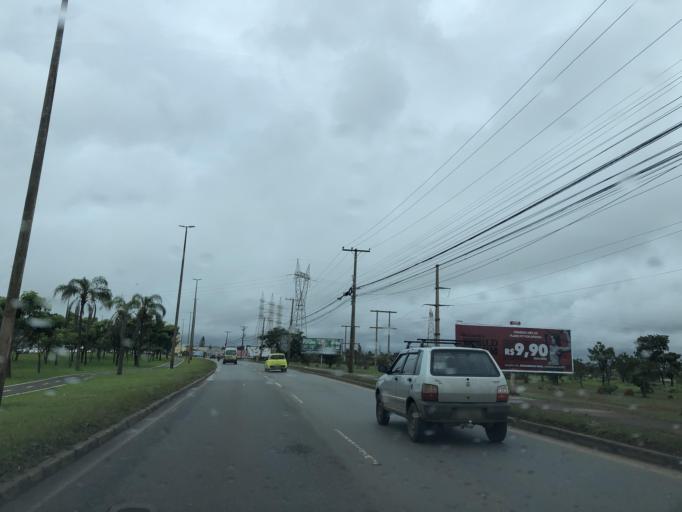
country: BR
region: Federal District
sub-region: Brasilia
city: Brasilia
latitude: -15.8625
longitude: -48.0586
